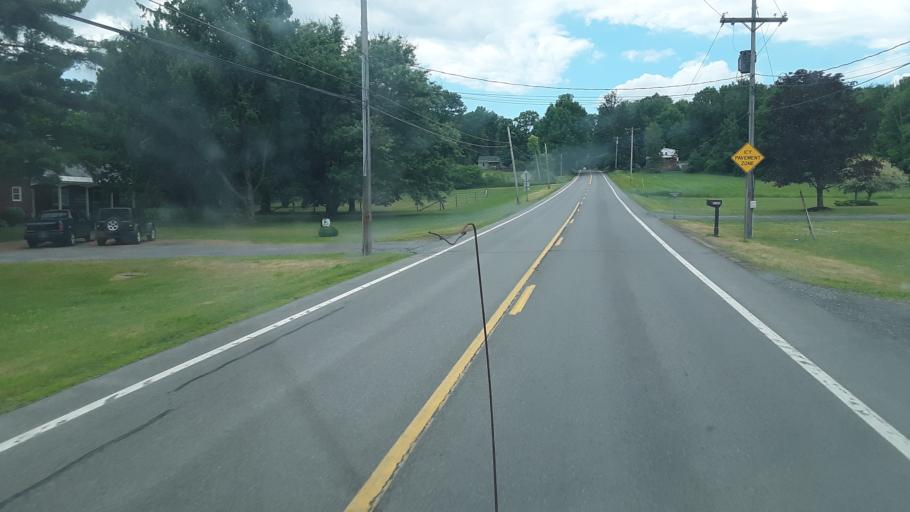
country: US
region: New York
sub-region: Oneida County
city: Rome
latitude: 43.3136
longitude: -75.4748
